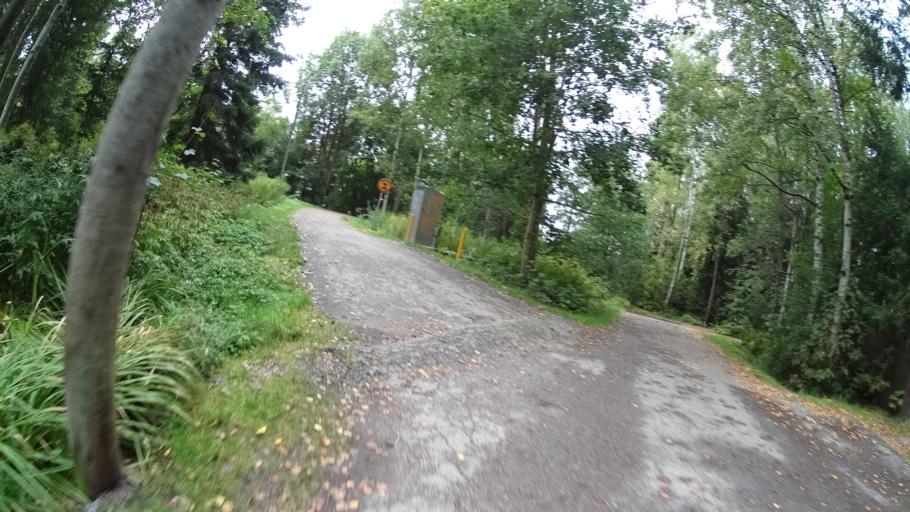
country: FI
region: Uusimaa
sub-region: Helsinki
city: Kauniainen
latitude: 60.2183
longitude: 24.7348
